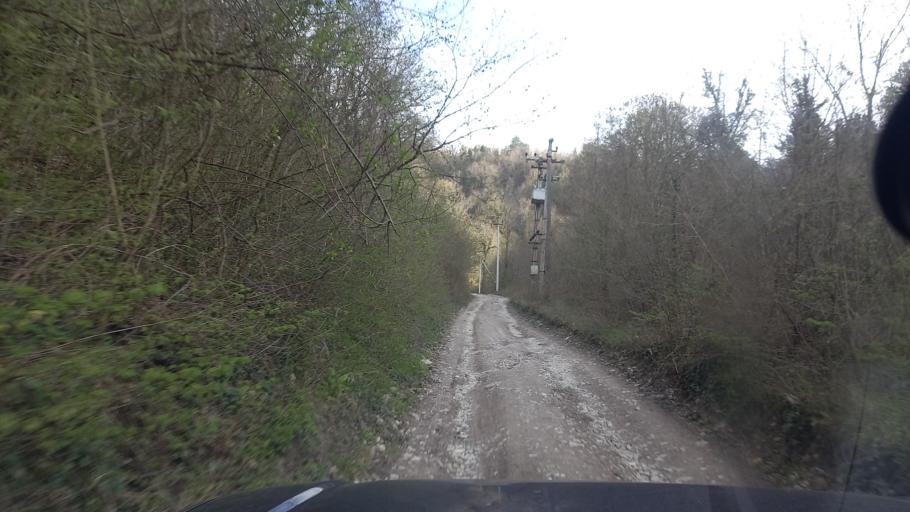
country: RU
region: Krasnodarskiy
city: Arkhipo-Osipovka
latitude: 44.3692
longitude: 38.5843
